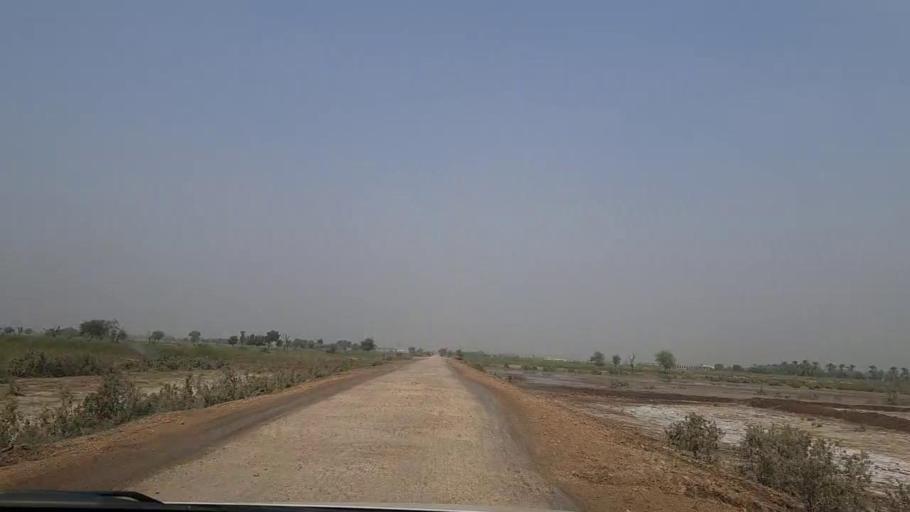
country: PK
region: Sindh
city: Pithoro
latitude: 25.5495
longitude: 69.2274
